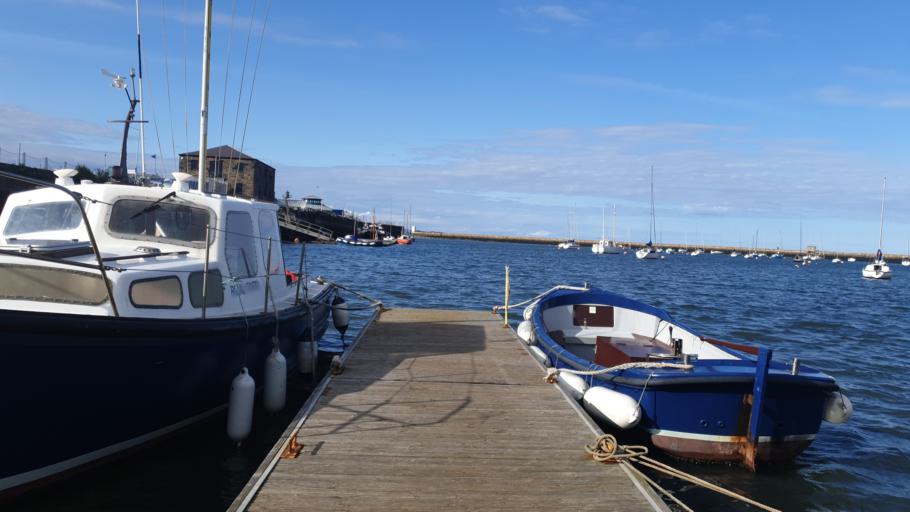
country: GB
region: Scotland
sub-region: Edinburgh
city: Edinburgh
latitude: 55.9832
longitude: -3.2227
